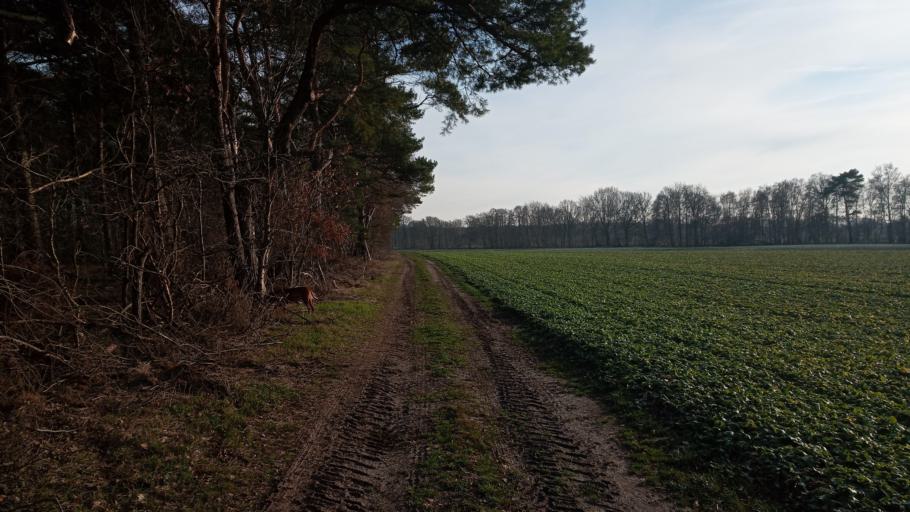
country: DE
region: Lower Saxony
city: Reessum
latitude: 53.1500
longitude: 9.2379
